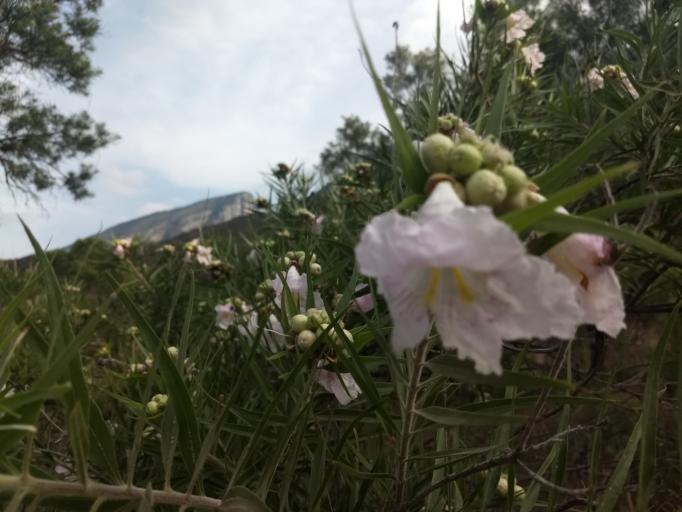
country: MX
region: Nuevo Leon
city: Santiago
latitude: 25.4038
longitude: -100.3127
